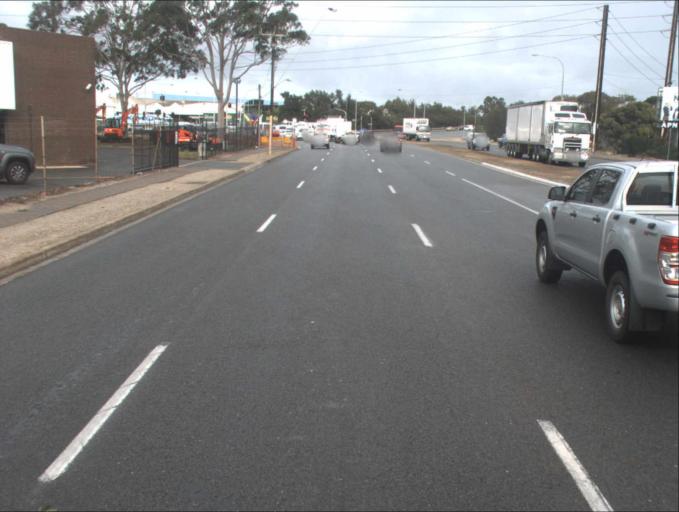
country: AU
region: South Australia
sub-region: Port Adelaide Enfield
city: Blair Athol
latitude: -34.8478
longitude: 138.5836
